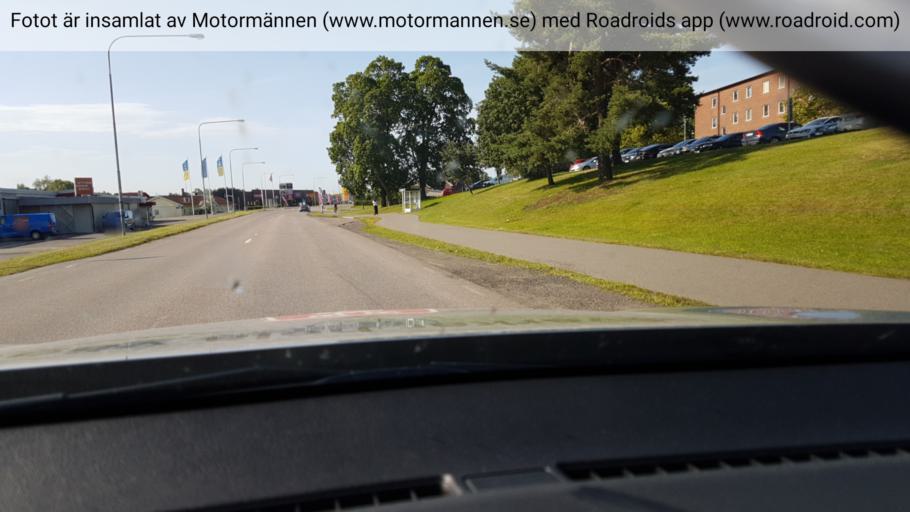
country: SE
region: Vaestra Goetaland
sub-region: Skovde Kommun
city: Skoevde
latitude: 58.4046
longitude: 13.8665
